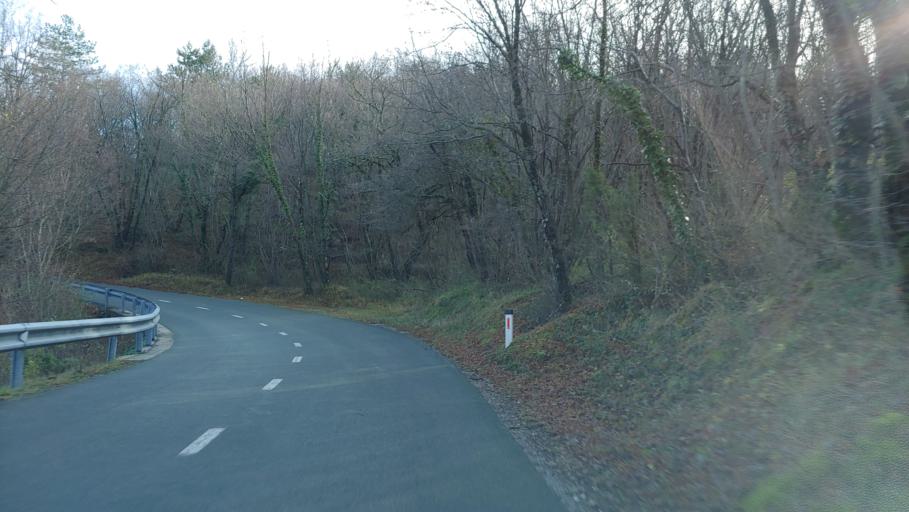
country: IT
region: Friuli Venezia Giulia
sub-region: Provincia di Trieste
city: Sistiana-Visogliano
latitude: 45.8102
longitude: 13.6496
